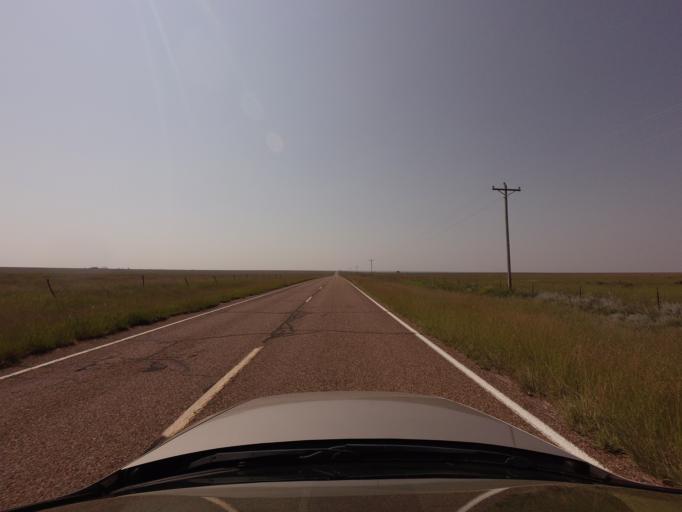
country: US
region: New Mexico
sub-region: Curry County
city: Cannon Air Force Base
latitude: 34.6867
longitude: -103.6354
